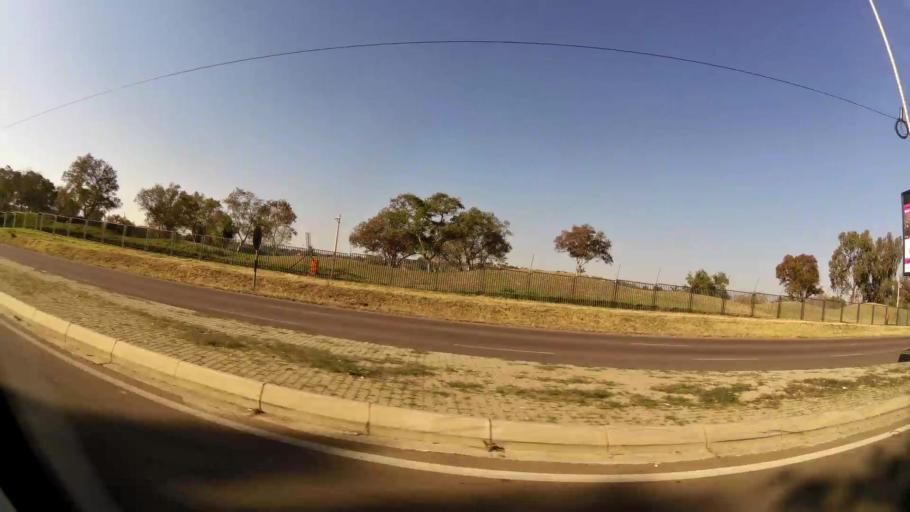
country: ZA
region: Gauteng
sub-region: City of Tshwane Metropolitan Municipality
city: Centurion
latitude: -25.8144
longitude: 28.3035
